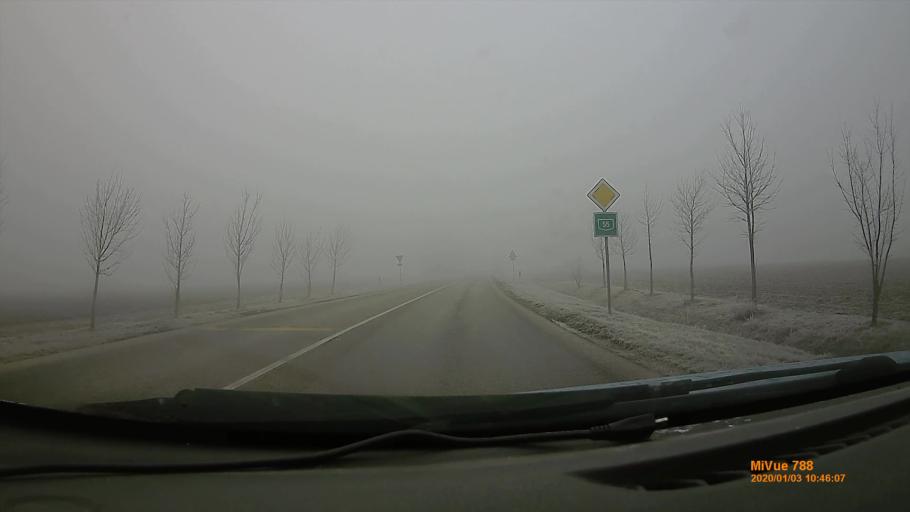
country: HU
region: Tolna
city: Bataszek
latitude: 46.2067
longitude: 18.7214
